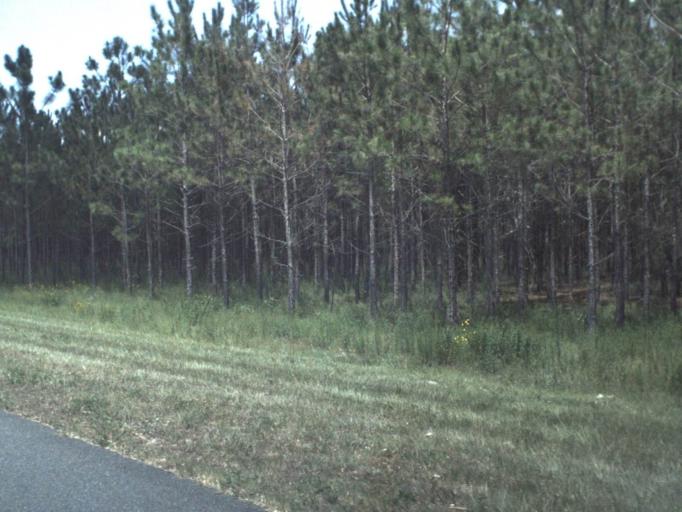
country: US
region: Florida
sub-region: Dixie County
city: Cross City
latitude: 29.7577
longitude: -82.9827
